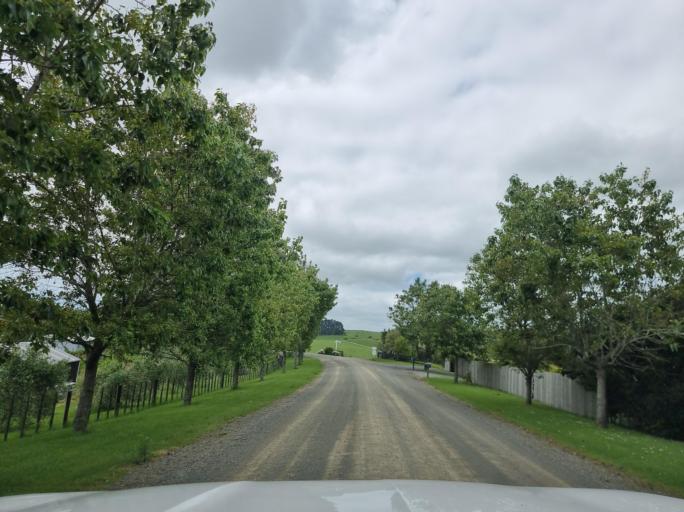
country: NZ
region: Auckland
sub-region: Auckland
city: Wellsford
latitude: -36.0942
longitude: 174.5323
